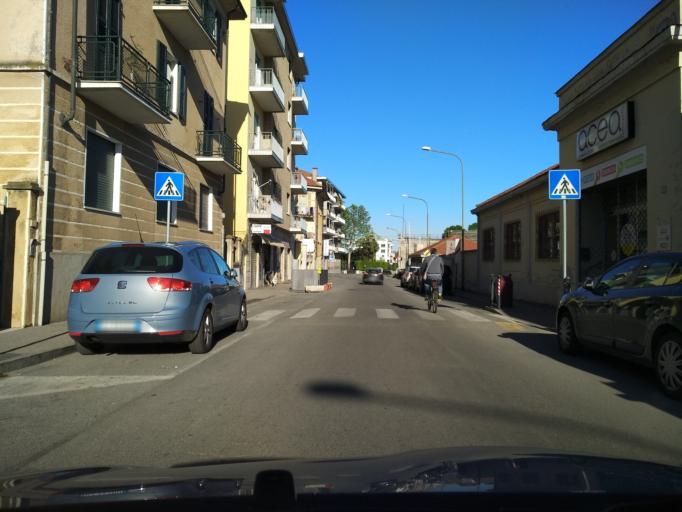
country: IT
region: Piedmont
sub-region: Provincia di Torino
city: Pinerolo
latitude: 44.8840
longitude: 7.3378
